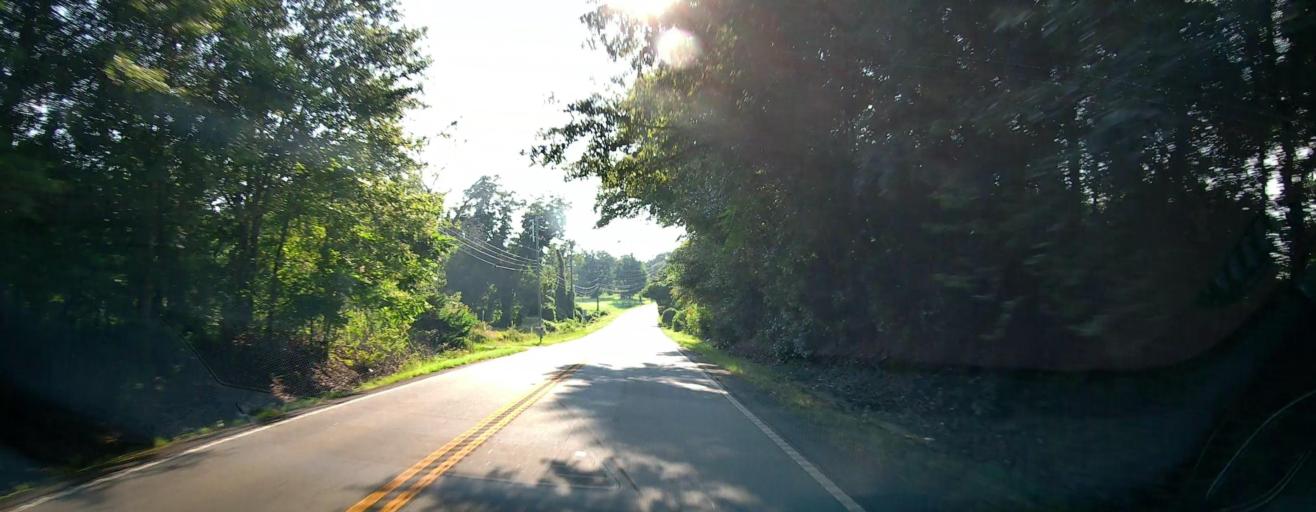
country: US
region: Georgia
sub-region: Houston County
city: Perry
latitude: 32.5029
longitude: -83.6331
